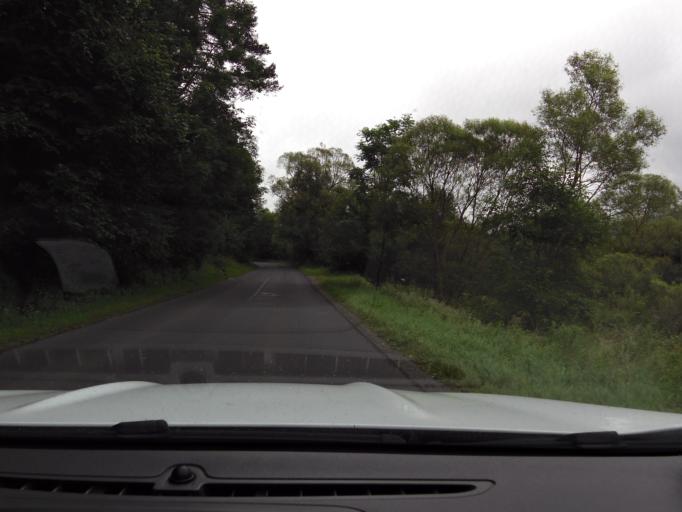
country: PL
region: Silesian Voivodeship
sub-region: Powiat zywiecki
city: Rajcza
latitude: 49.4932
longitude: 19.1130
